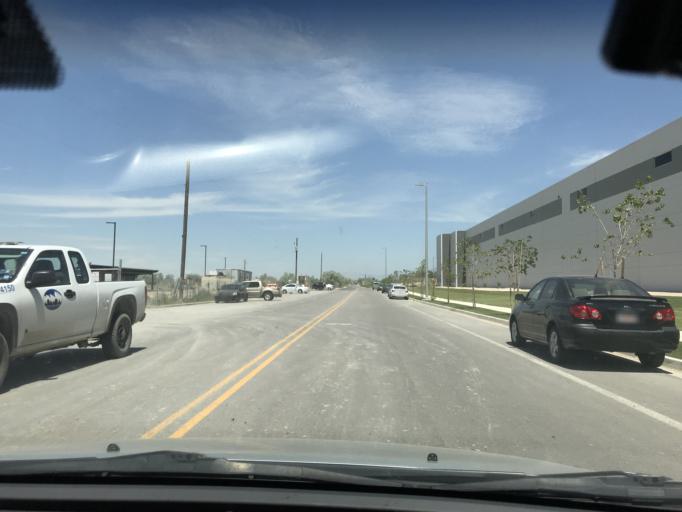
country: US
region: Utah
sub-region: Davis County
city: North Salt Lake
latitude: 40.8152
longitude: -111.9534
